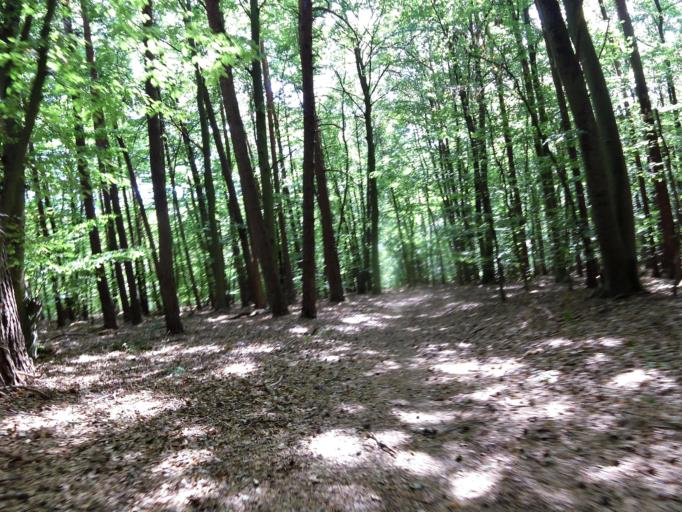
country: DE
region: Bavaria
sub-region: Regierungsbezirk Unterfranken
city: Theilheim
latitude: 49.7449
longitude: 10.0166
